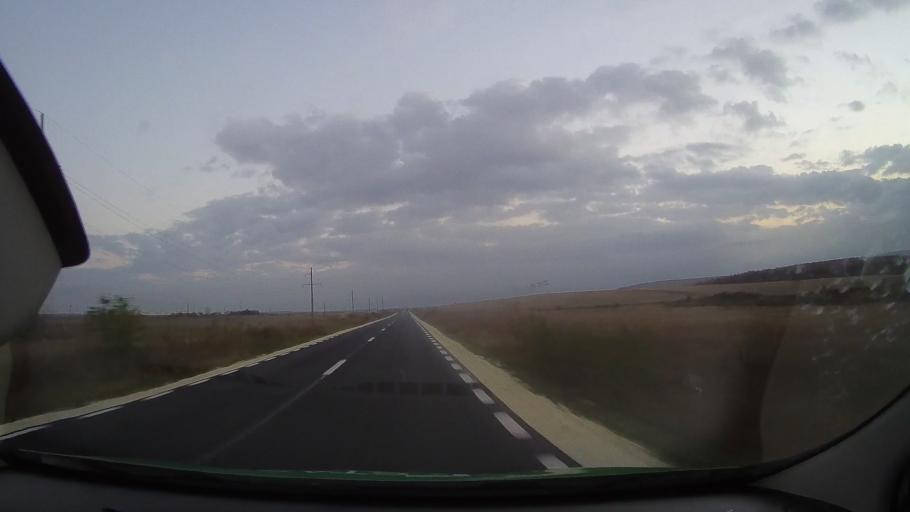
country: RO
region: Constanta
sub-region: Comuna Baneasa
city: Baneasa
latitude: 44.0882
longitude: 27.6877
